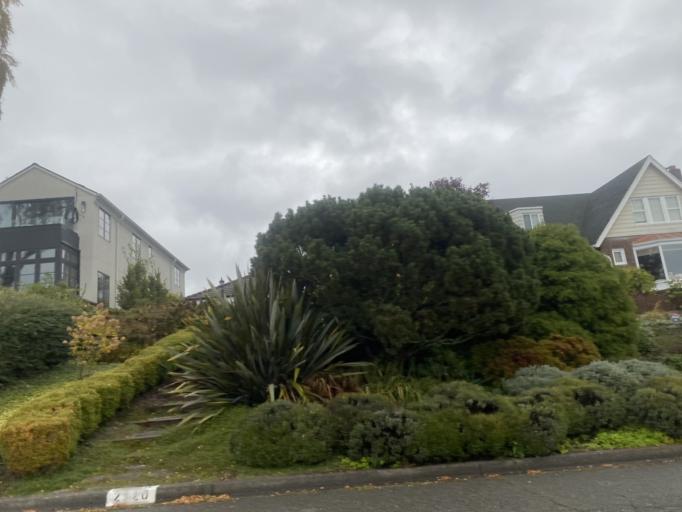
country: US
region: Washington
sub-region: King County
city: Seattle
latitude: 47.6417
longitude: -122.4135
